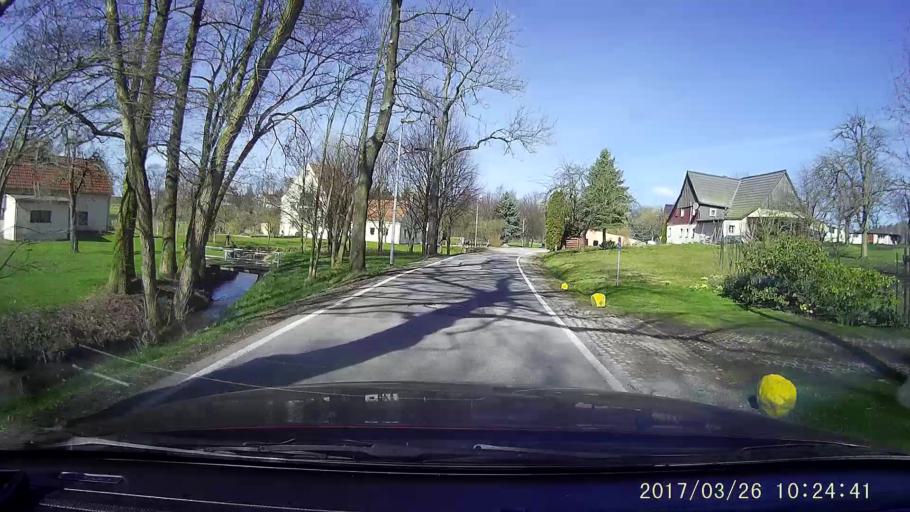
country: DE
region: Saxony
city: Sohland am Rotstein
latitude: 51.1040
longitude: 14.7371
